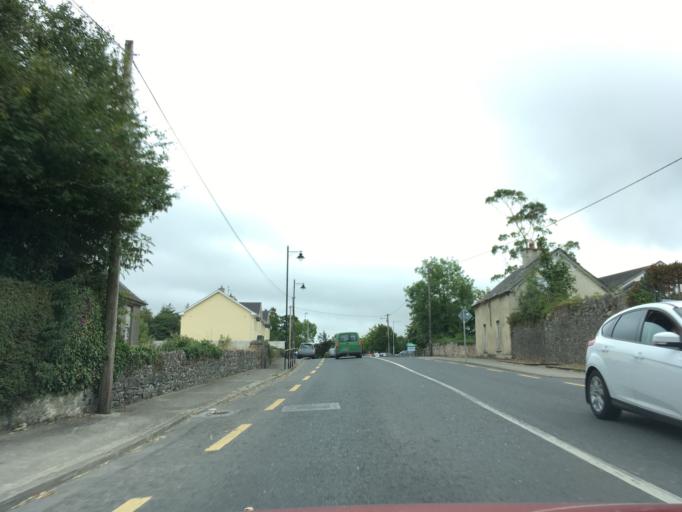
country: IE
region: Munster
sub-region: South Tipperary
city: Cluain Meala
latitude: 52.4121
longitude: -7.7548
